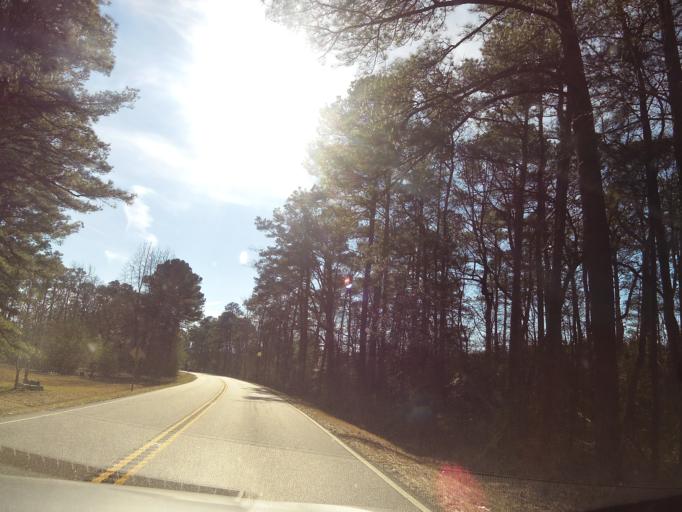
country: US
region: Virginia
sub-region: Isle of Wight County
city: Isle of Wight
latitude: 36.8878
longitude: -76.7320
